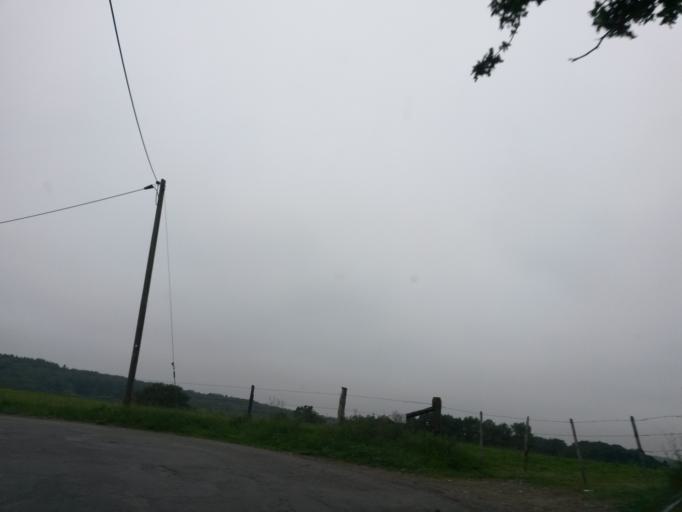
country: DE
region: North Rhine-Westphalia
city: Meinerzhagen
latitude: 51.1095
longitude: 7.6219
